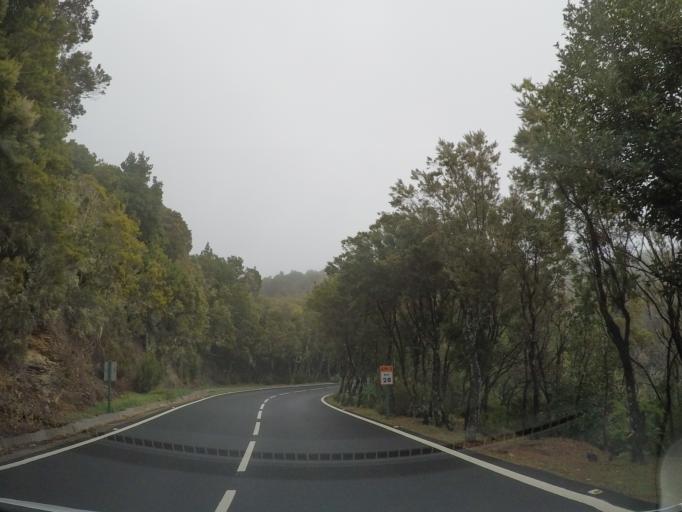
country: ES
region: Canary Islands
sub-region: Provincia de Santa Cruz de Tenerife
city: Vallehermosa
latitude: 28.1286
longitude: -17.2684
